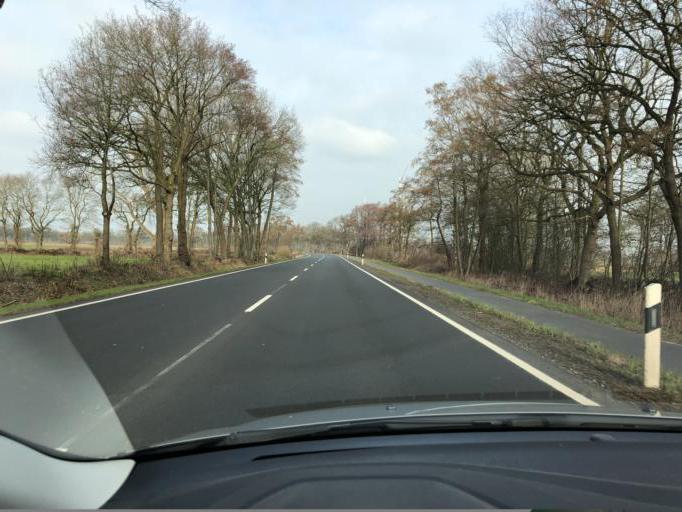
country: DE
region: Lower Saxony
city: Mittegrossefehn
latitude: 53.3558
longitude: 7.5997
